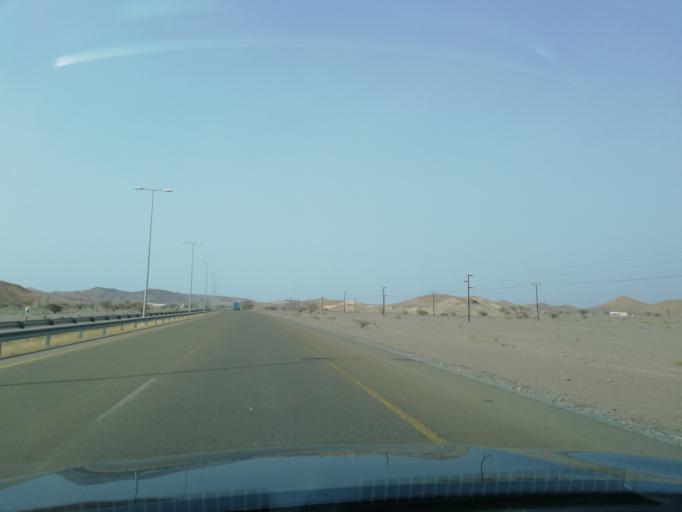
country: OM
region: Al Batinah
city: Al Liwa'
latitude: 24.3627
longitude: 56.5305
